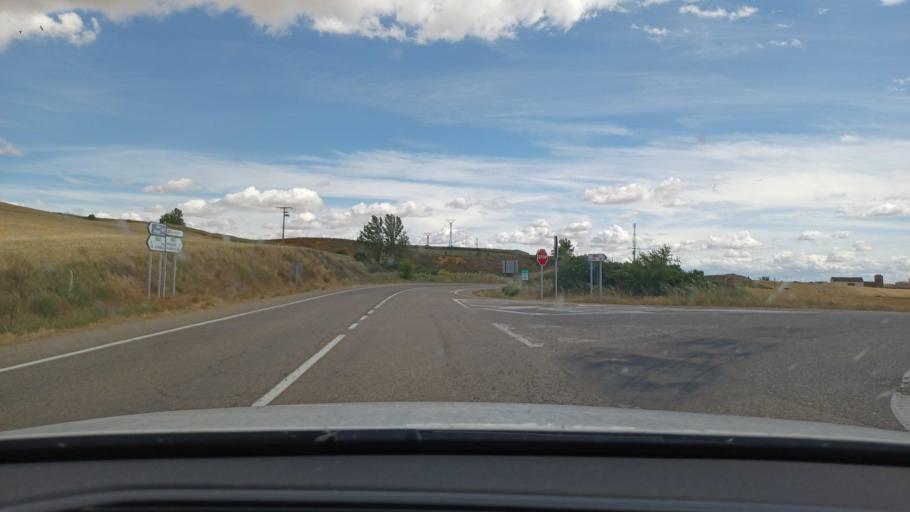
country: ES
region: Castille and Leon
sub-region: Provincia de Leon
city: Sahagun
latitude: 42.3802
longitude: -5.0271
